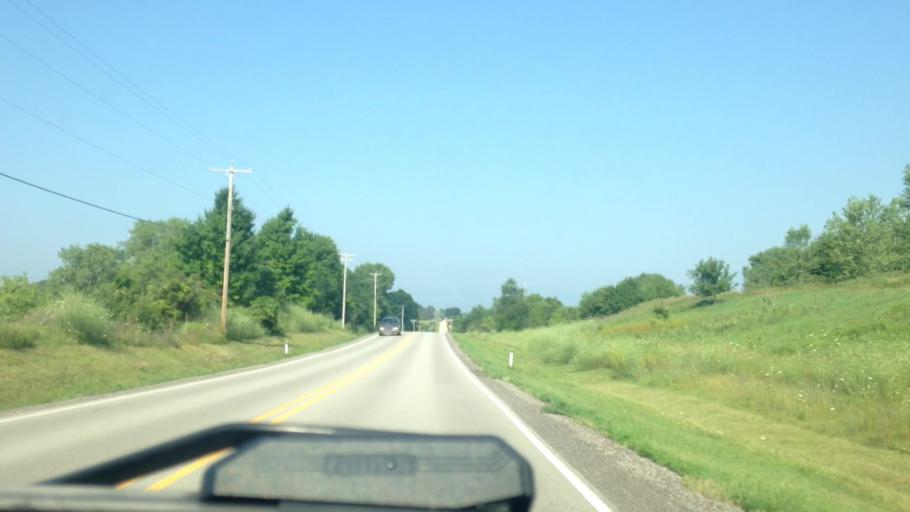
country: US
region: Wisconsin
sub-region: Waukesha County
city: Merton
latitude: 43.1631
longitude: -88.2806
